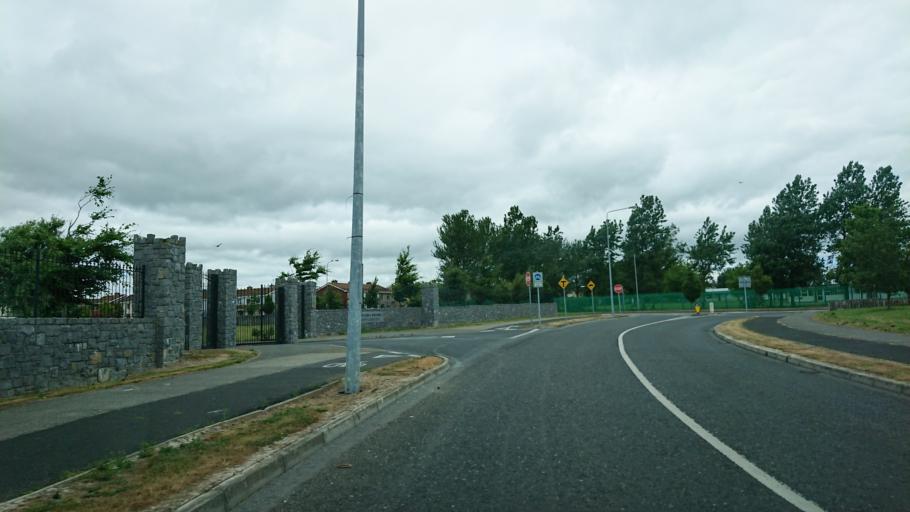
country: IE
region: Munster
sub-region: Waterford
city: Waterford
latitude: 52.2387
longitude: -7.1455
